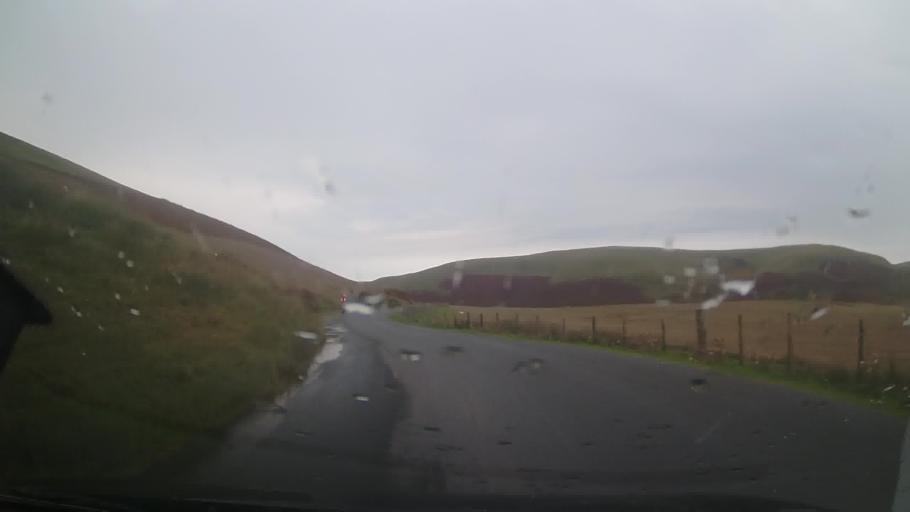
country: GB
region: Wales
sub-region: Sir Powys
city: Rhayader
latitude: 52.3285
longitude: -3.6234
